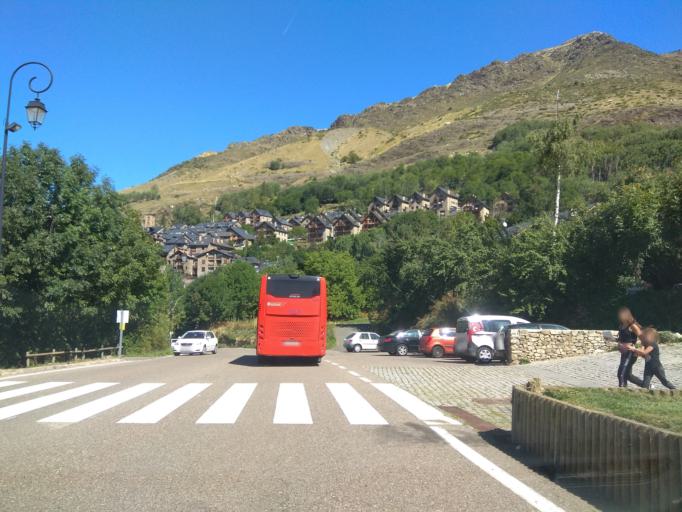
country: ES
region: Catalonia
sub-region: Provincia de Lleida
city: Vielha
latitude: 42.5178
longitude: 0.8479
